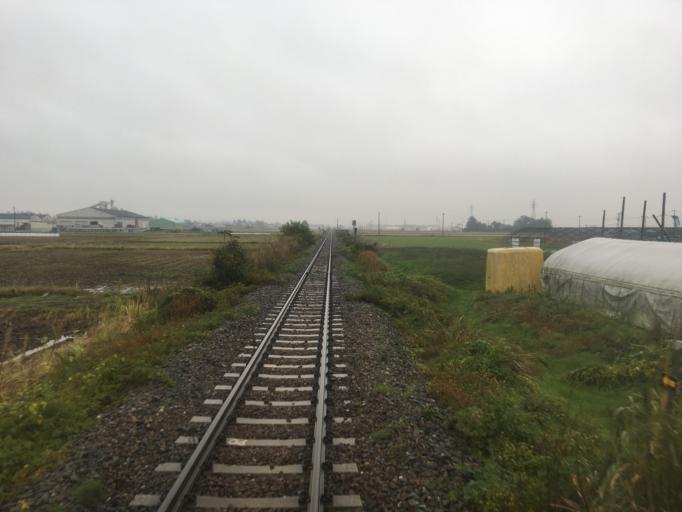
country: JP
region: Miyagi
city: Furukawa
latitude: 38.5647
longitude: 141.0017
